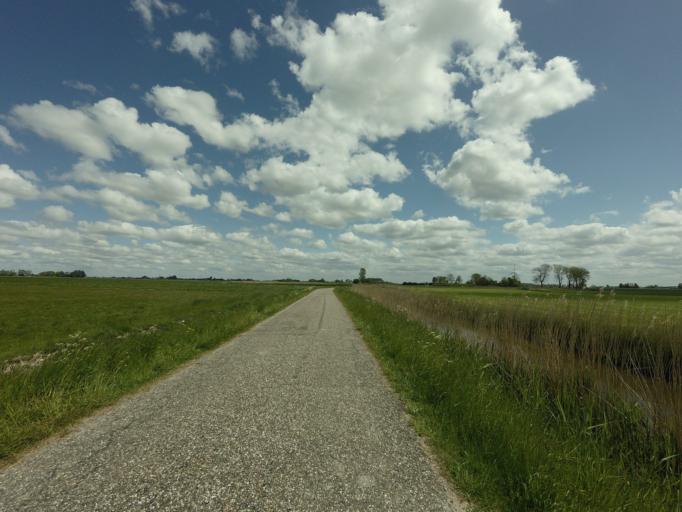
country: NL
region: Friesland
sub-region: Gemeente Franekeradeel
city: Franeker
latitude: 53.1456
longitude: 5.5013
